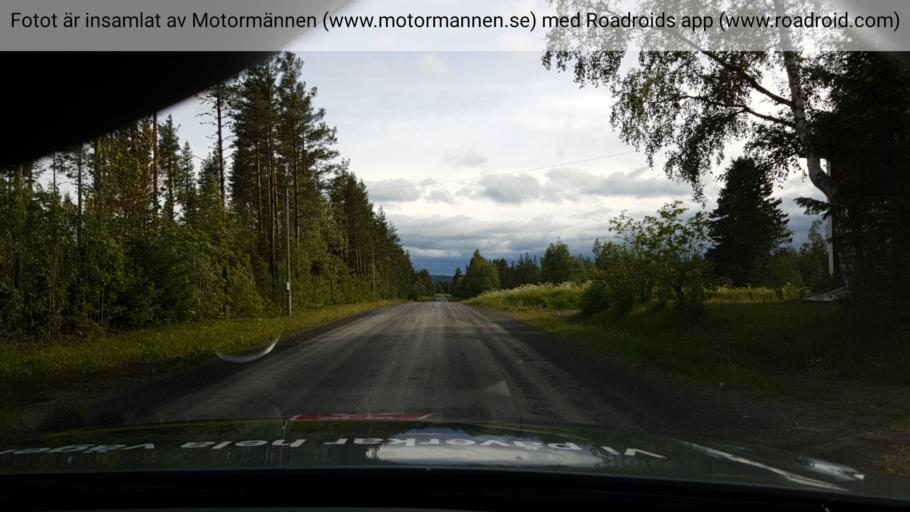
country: SE
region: Jaemtland
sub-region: Stroemsunds Kommun
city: Stroemsund
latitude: 63.6873
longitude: 15.1225
